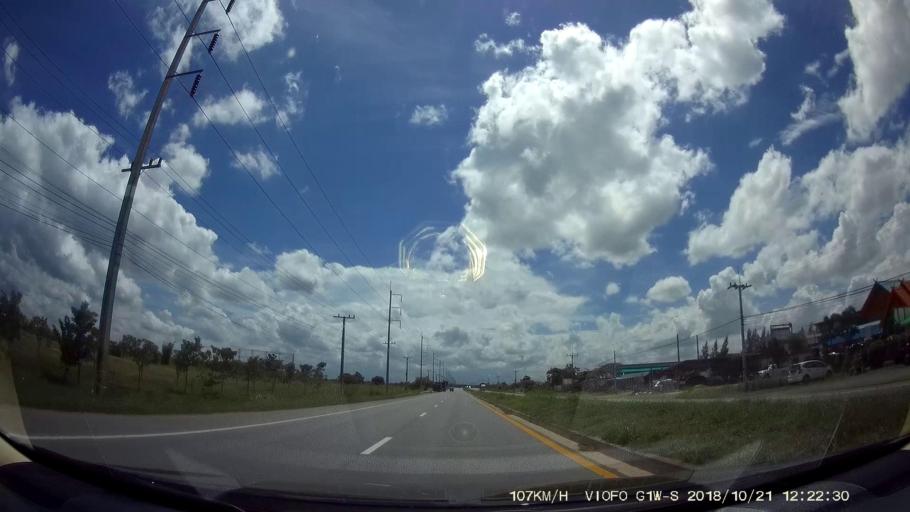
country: TH
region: Nakhon Ratchasima
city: Dan Khun Thot
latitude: 15.2603
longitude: 101.7895
